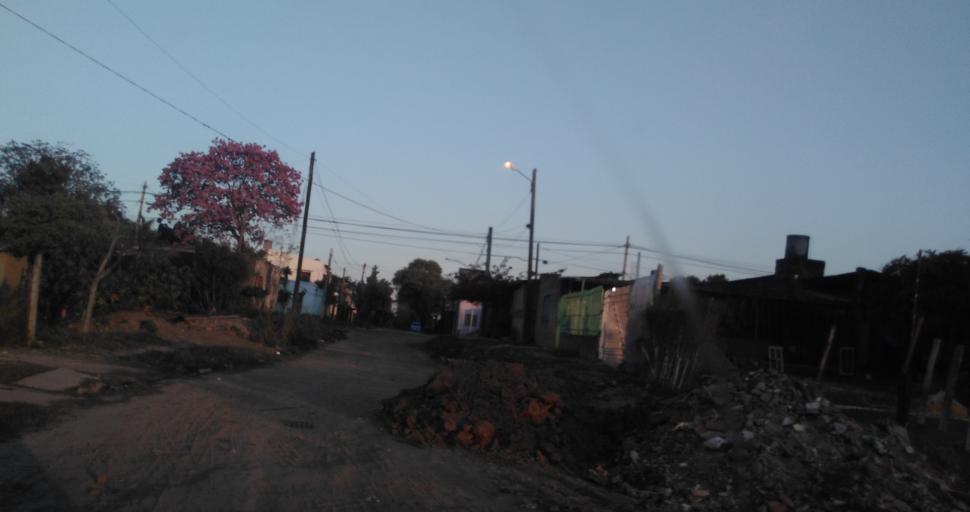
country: AR
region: Chaco
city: Fontana
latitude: -27.4303
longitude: -58.9981
